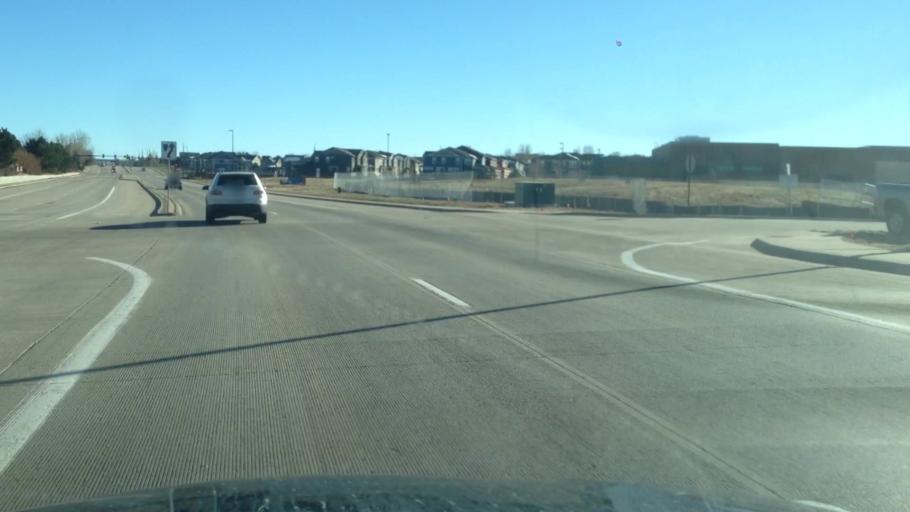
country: US
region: Colorado
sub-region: Arapahoe County
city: Dove Valley
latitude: 39.5710
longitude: -104.8050
